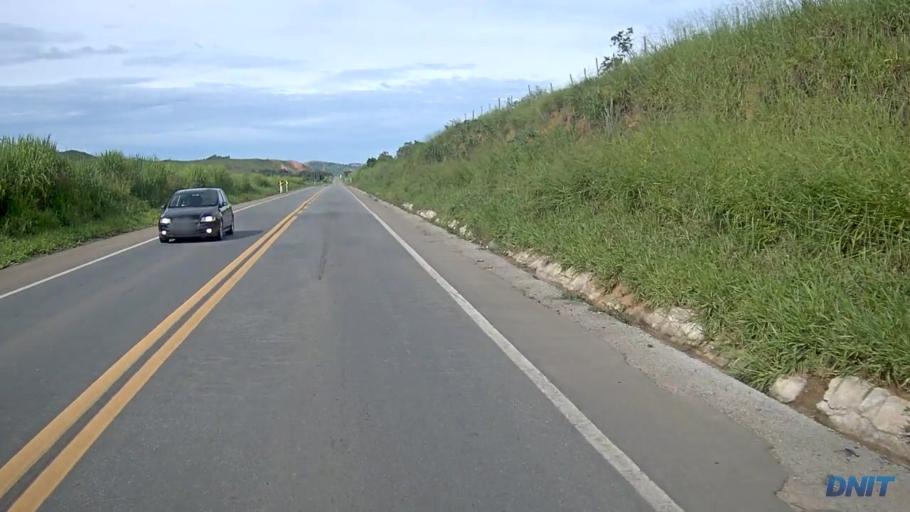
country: BR
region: Minas Gerais
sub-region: Belo Oriente
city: Belo Oriente
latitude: -19.1972
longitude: -42.2837
